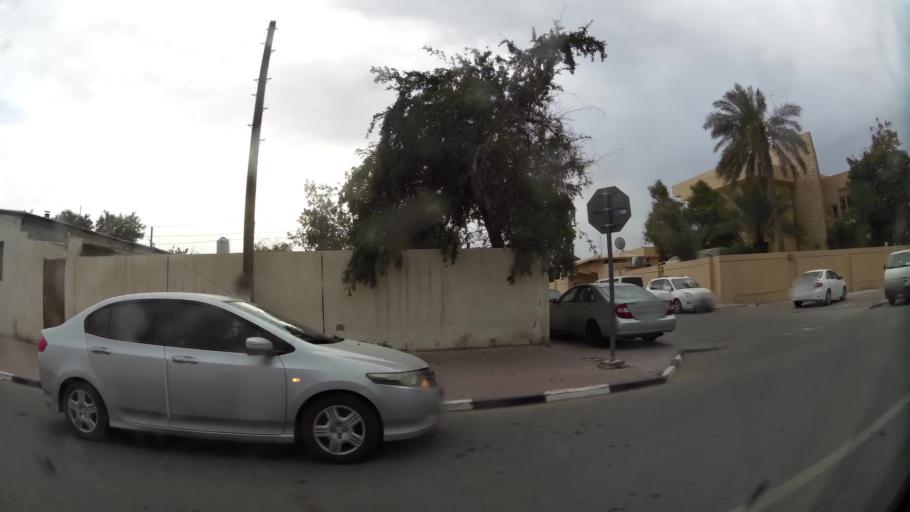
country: QA
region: Baladiyat ad Dawhah
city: Doha
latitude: 25.2698
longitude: 51.4960
